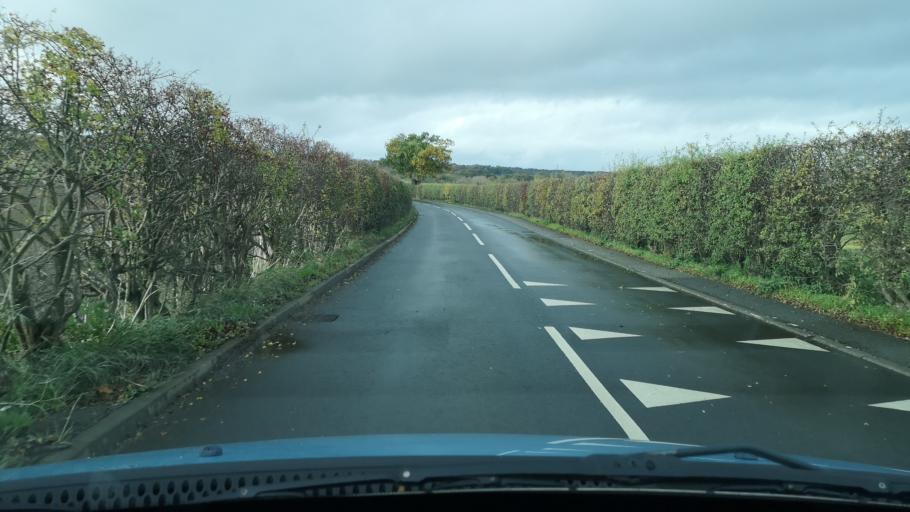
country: GB
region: England
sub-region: City and Borough of Wakefield
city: Notton
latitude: 53.6121
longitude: -1.4881
